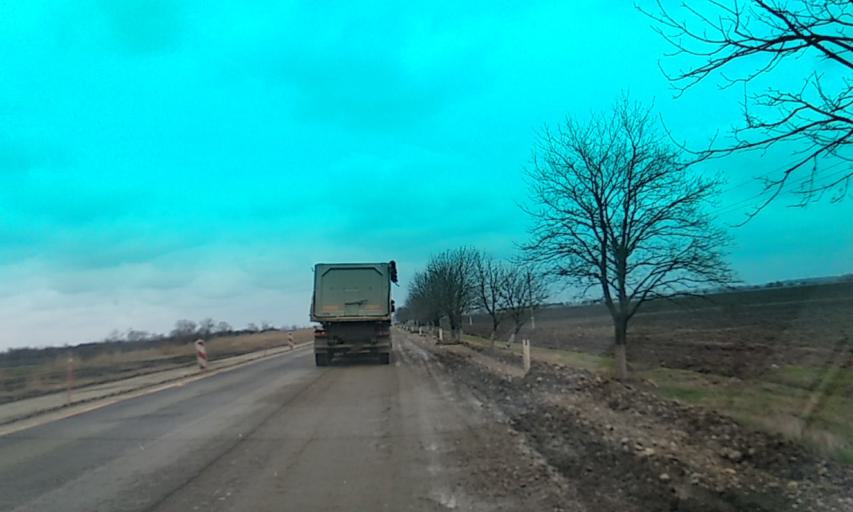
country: RU
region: Krasnodarskiy
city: Velikovechnoye
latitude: 44.9957
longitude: 39.7108
